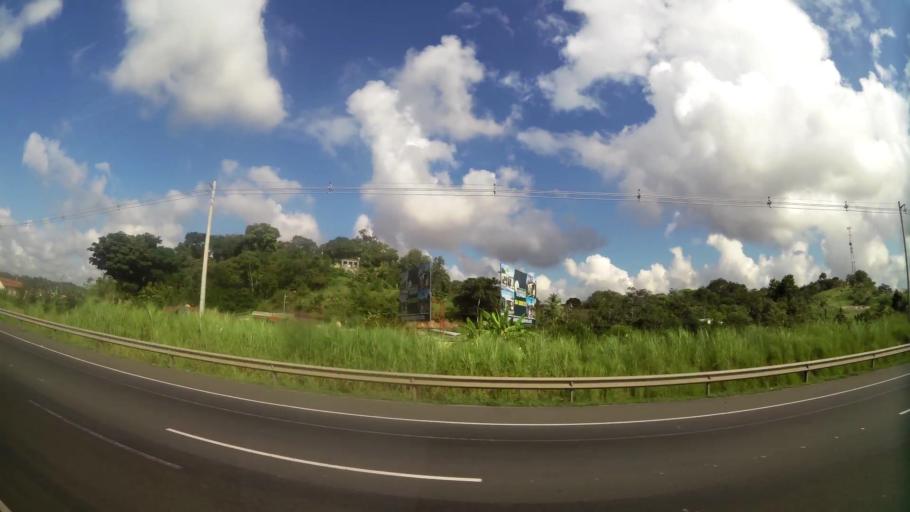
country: PA
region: Panama
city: Nuevo Arraijan
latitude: 8.9150
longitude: -79.7154
